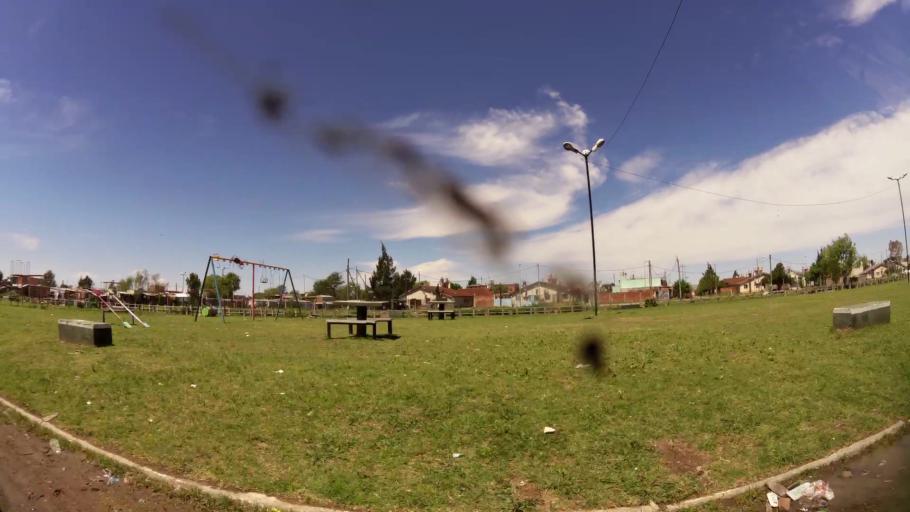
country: AR
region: Buenos Aires
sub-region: Partido de Quilmes
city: Quilmes
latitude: -34.7439
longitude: -58.3095
